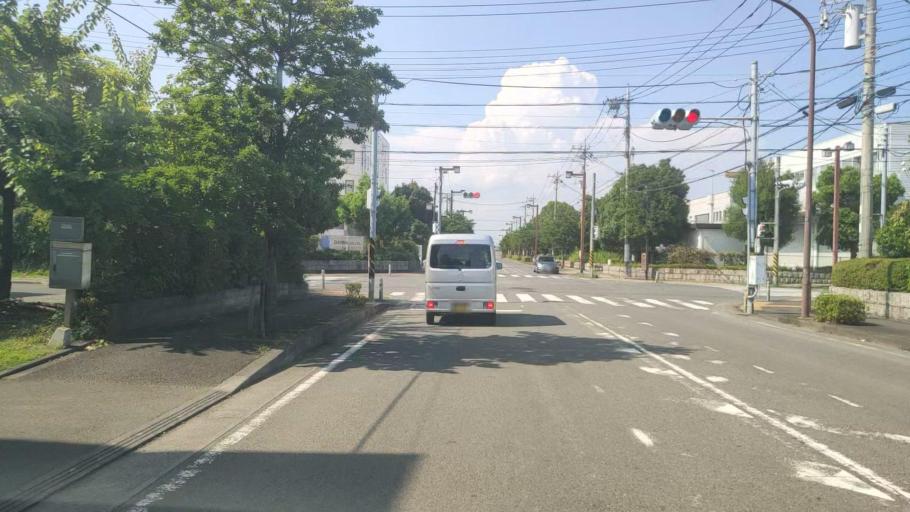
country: JP
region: Kanagawa
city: Hiratsuka
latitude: 35.3589
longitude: 139.3399
